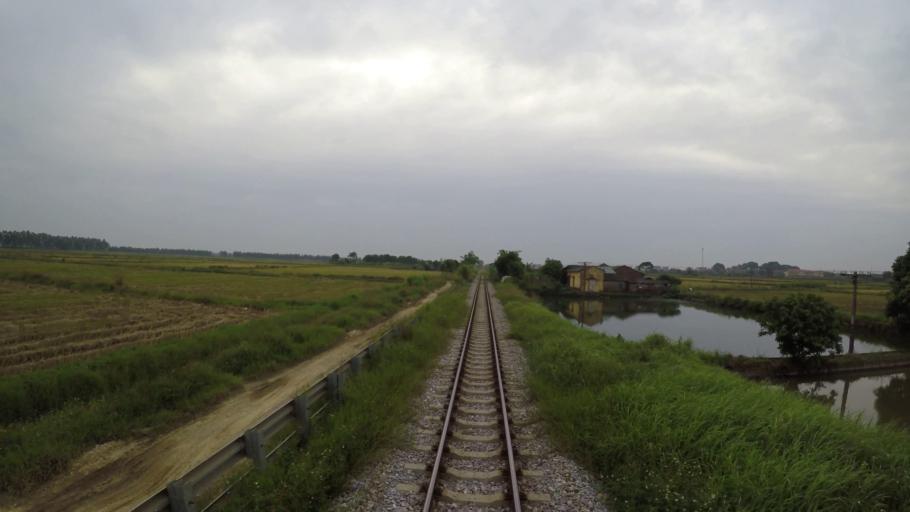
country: VN
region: Bac Ninh
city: Thua
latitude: 20.9648
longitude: 106.1757
